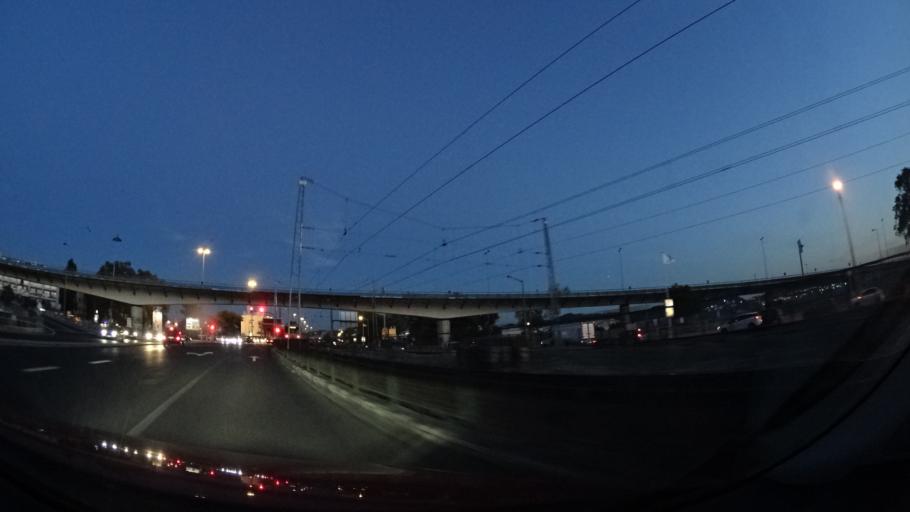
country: PT
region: Lisbon
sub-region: Oeiras
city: Alges
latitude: 38.6982
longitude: -9.2280
